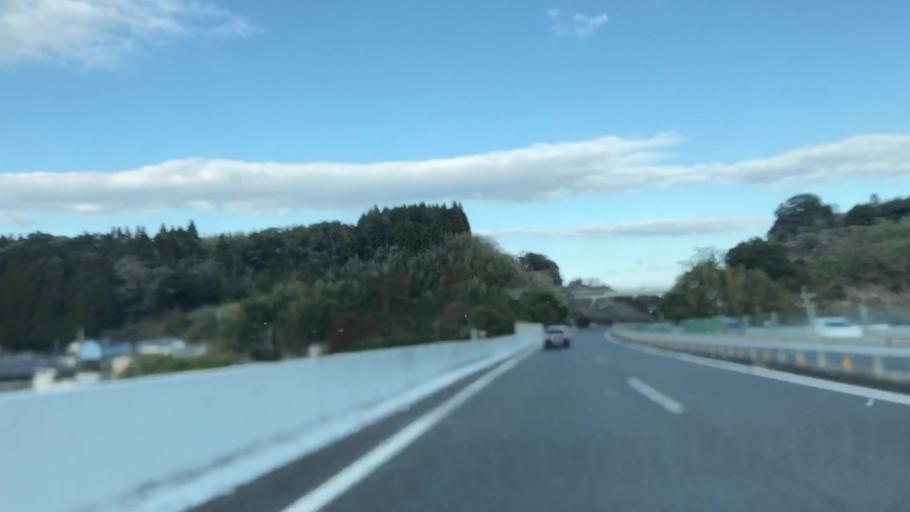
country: JP
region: Miyazaki
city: Miyazaki-shi
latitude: 31.8629
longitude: 131.3817
